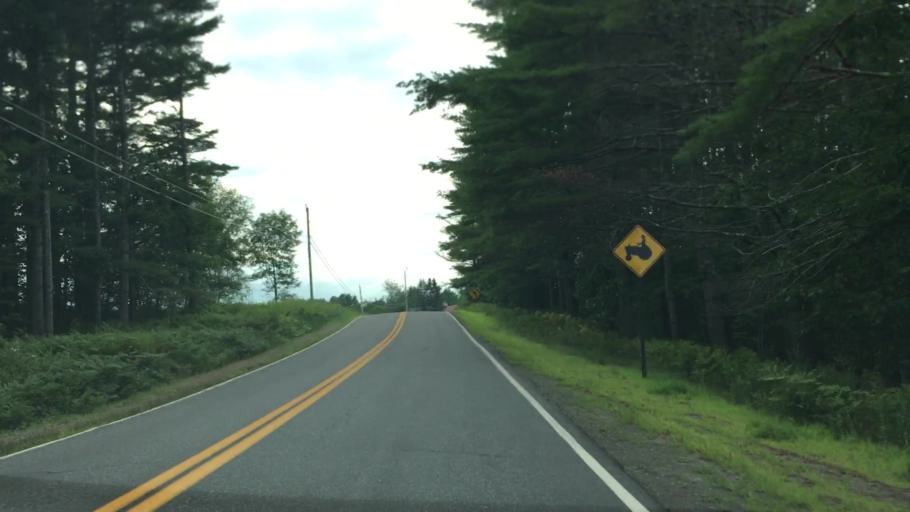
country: US
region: Maine
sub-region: Waldo County
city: Lincolnville
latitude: 44.3221
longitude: -69.0712
